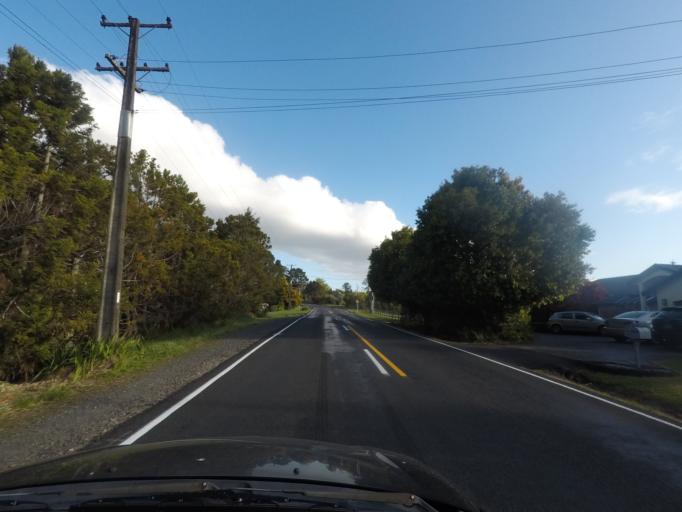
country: NZ
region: Auckland
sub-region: Auckland
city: Waitakere
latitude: -36.9167
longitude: 174.6150
